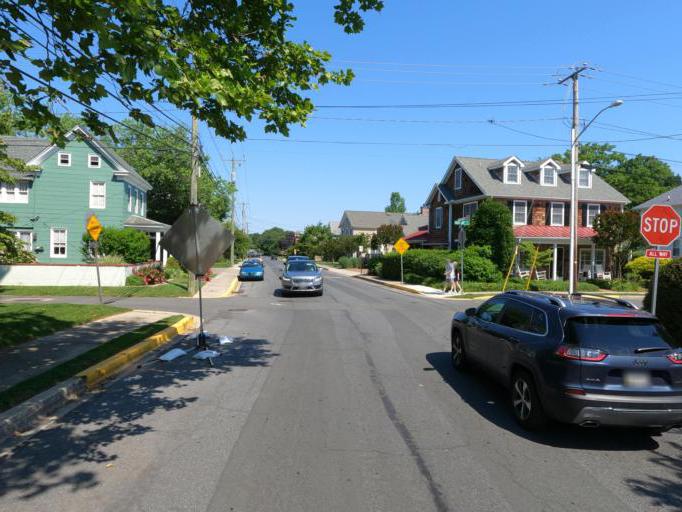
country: US
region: Delaware
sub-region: Sussex County
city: Lewes
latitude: 38.7737
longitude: -75.1433
